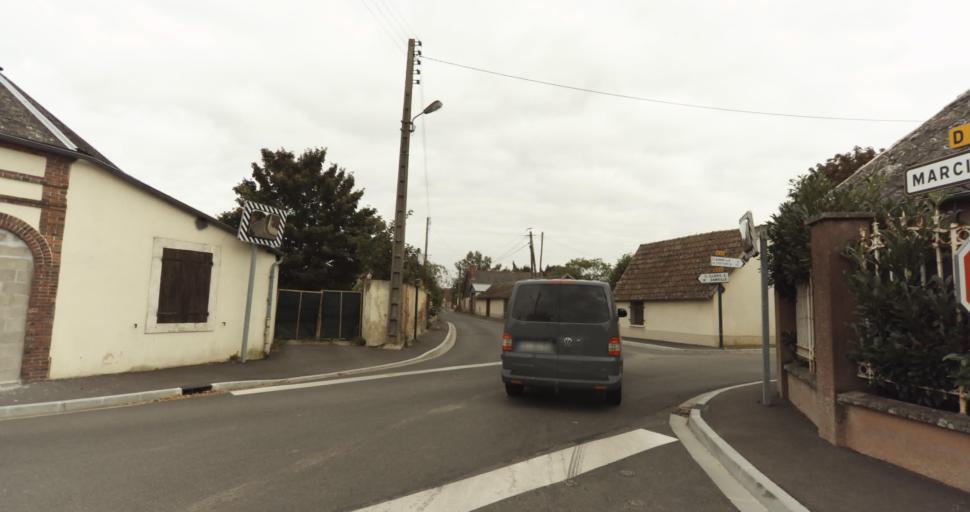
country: FR
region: Haute-Normandie
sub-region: Departement de l'Eure
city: Saint-Germain-sur-Avre
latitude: 48.8169
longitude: 1.2874
